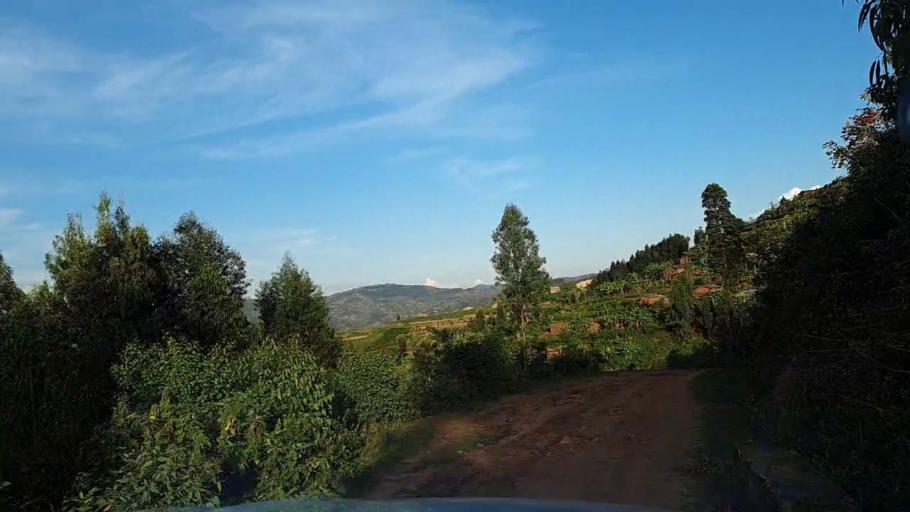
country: RW
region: Southern Province
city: Gikongoro
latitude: -2.4036
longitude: 29.5538
